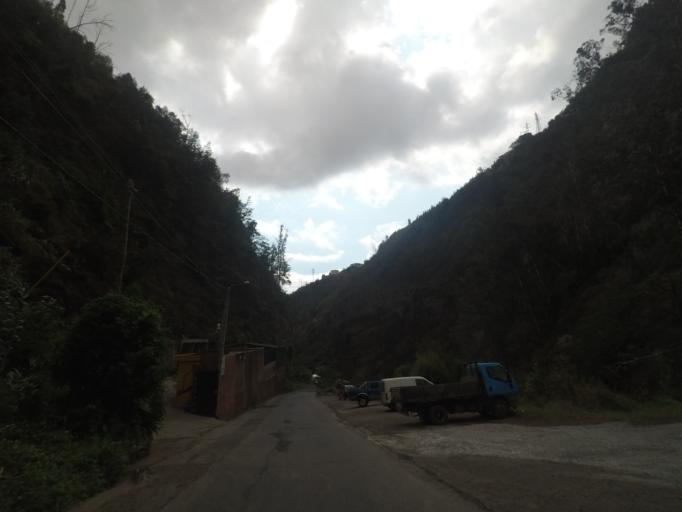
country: PT
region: Madeira
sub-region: Funchal
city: Nossa Senhora do Monte
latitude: 32.6799
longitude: -16.9167
